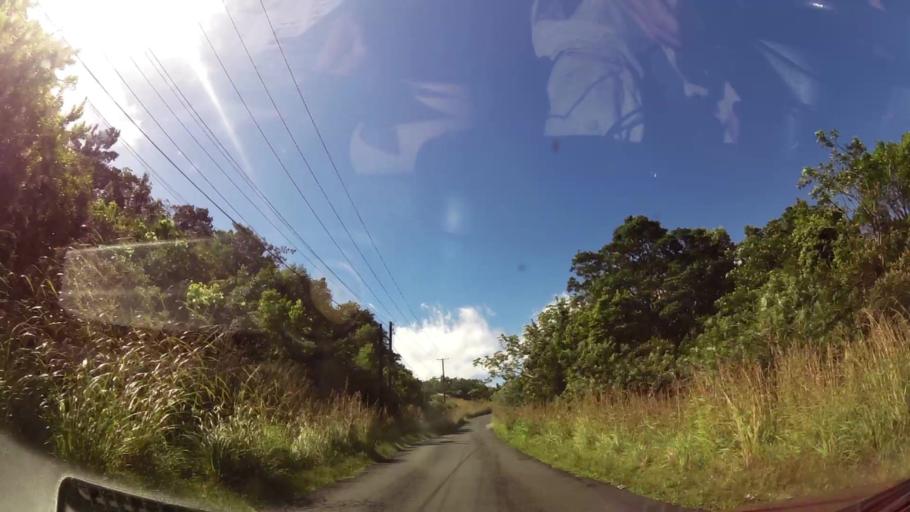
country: DM
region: Saint Paul
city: Pont Casse
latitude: 15.3831
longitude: -61.3386
